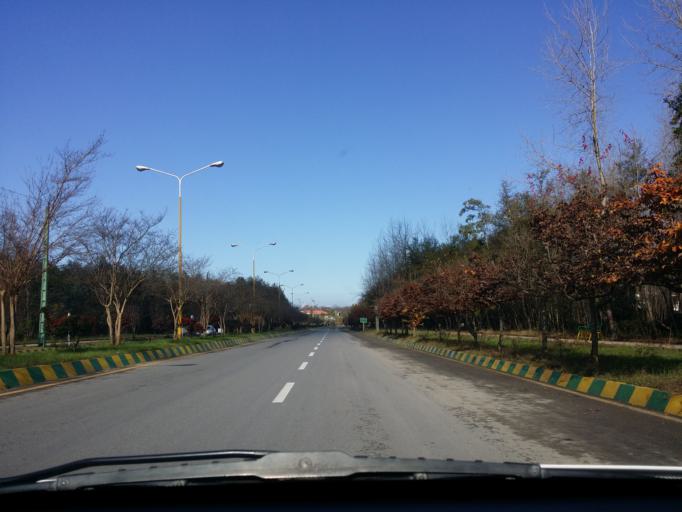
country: IR
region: Mazandaran
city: Chalus
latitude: 36.6790
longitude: 51.3063
